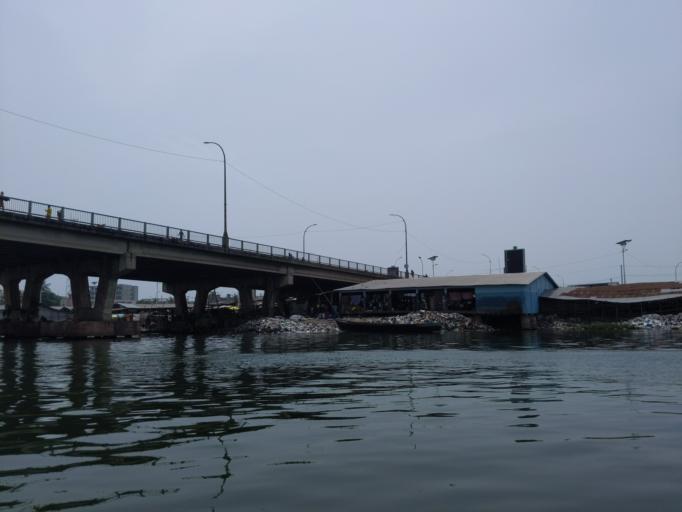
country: BJ
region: Littoral
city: Cotonou
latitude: 6.3714
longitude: 2.4364
